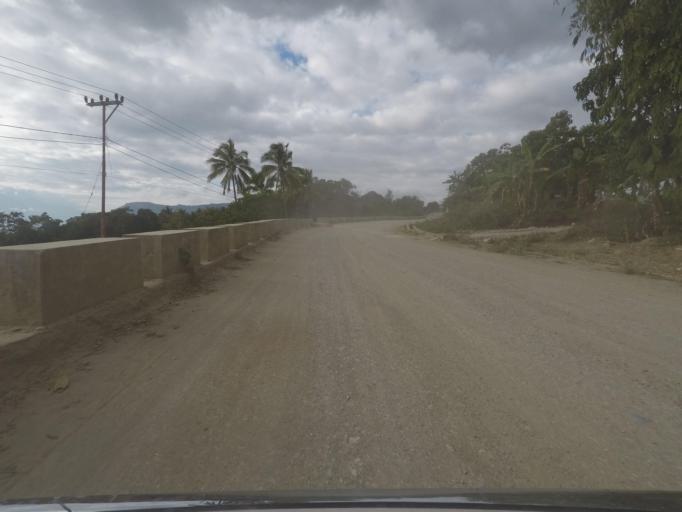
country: TL
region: Baucau
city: Venilale
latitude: -8.5949
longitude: 126.3852
